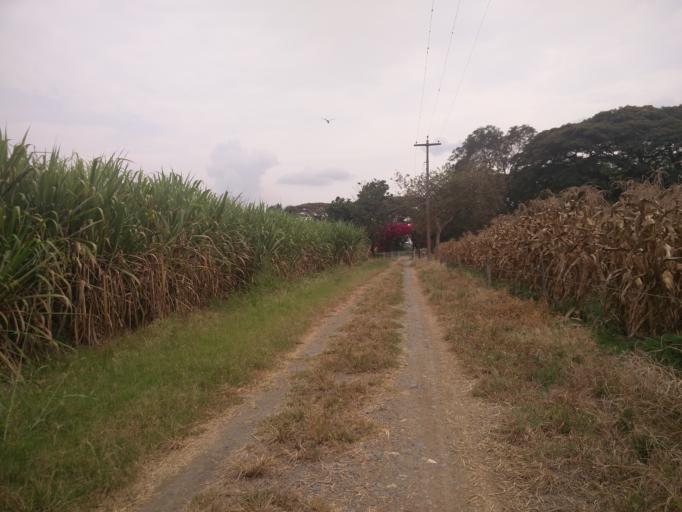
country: CO
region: Valle del Cauca
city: Buga
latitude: 3.8879
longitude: -76.3243
